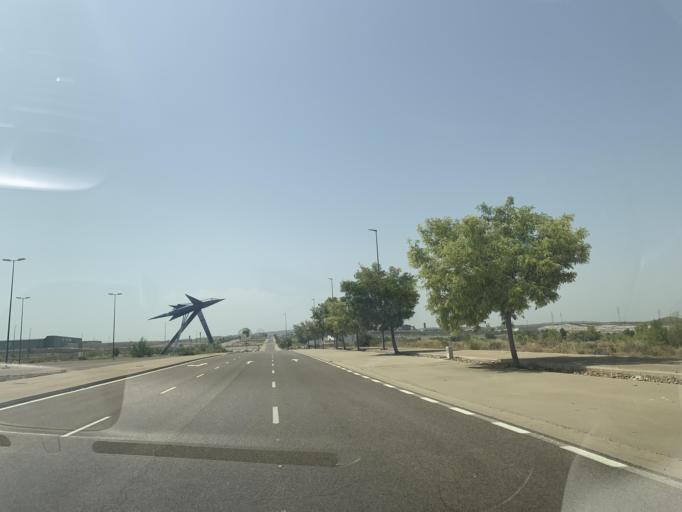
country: ES
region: Aragon
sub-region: Provincia de Zaragoza
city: Zaragoza
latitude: 41.5846
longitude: -0.8403
